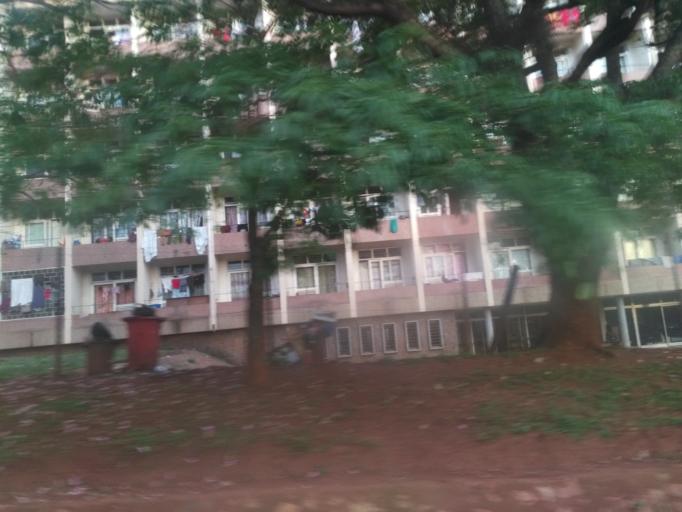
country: UG
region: Central Region
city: Kampala Central Division
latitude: 0.3372
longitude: 32.5773
